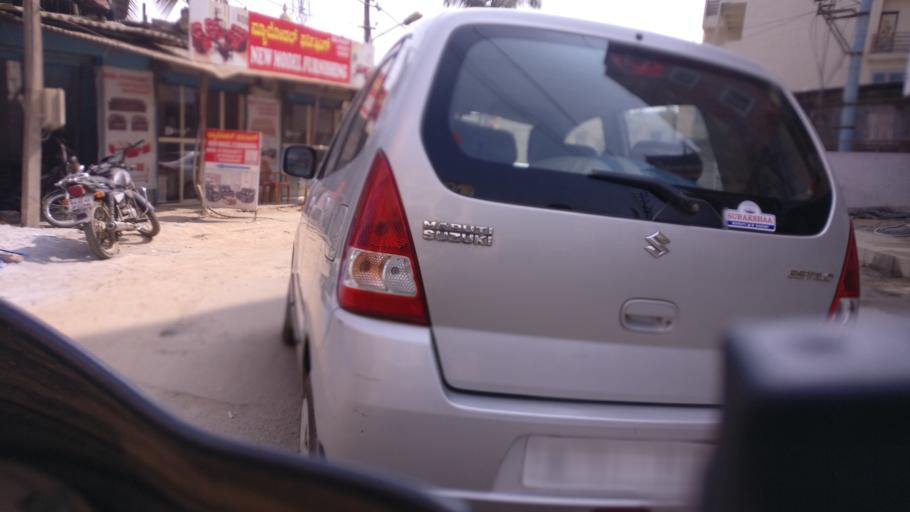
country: IN
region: Karnataka
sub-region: Bangalore Urban
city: Bangalore
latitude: 12.9132
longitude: 77.6768
